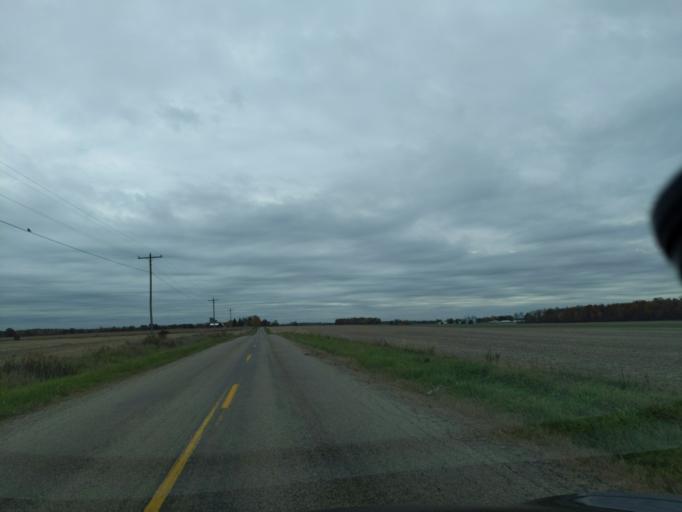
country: US
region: Michigan
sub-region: Eaton County
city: Eaton Rapids
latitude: 42.4494
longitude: -84.6006
